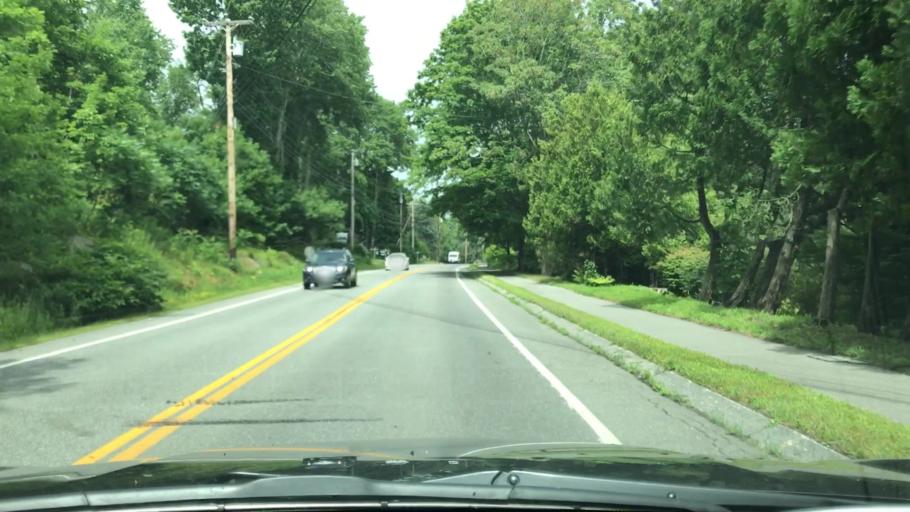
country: US
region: Maine
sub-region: Knox County
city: Camden
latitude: 44.2232
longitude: -69.0517
